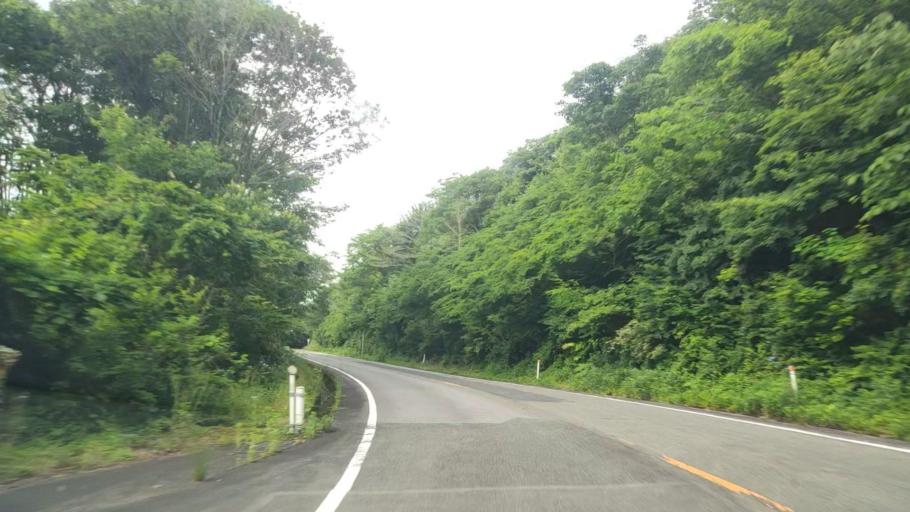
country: JP
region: Tottori
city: Kurayoshi
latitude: 35.3265
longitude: 133.5900
